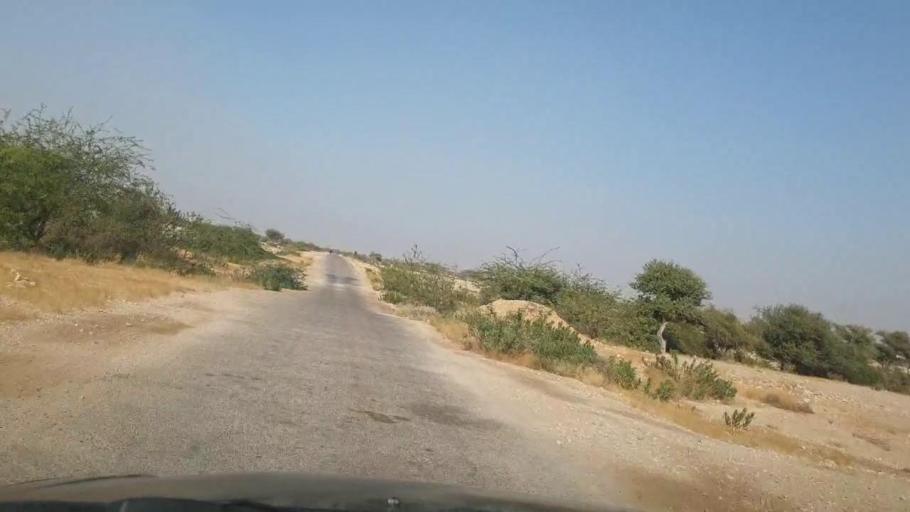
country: PK
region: Sindh
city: Jamshoro
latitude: 25.5480
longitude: 67.8276
